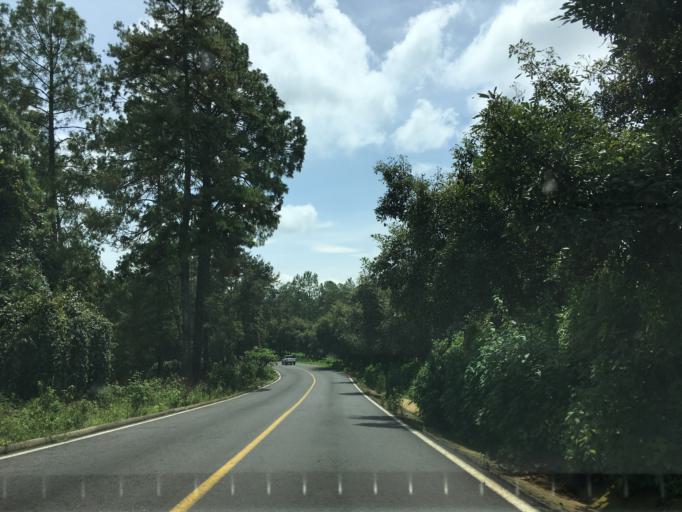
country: MX
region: Michoacan
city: Nuevo San Juan Parangaricutiro
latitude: 19.4431
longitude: -102.1649
